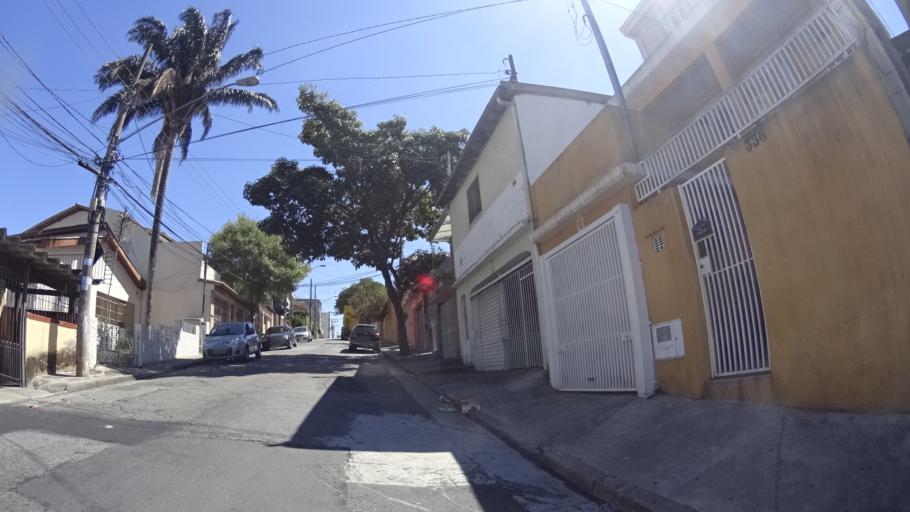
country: BR
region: Sao Paulo
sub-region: Sao Paulo
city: Sao Paulo
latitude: -23.4889
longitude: -46.6665
